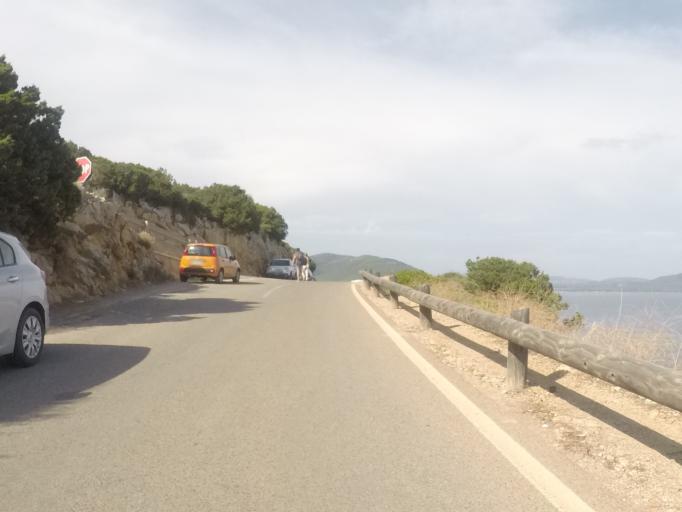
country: IT
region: Sardinia
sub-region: Provincia di Sassari
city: Alghero
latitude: 40.5645
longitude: 8.1644
